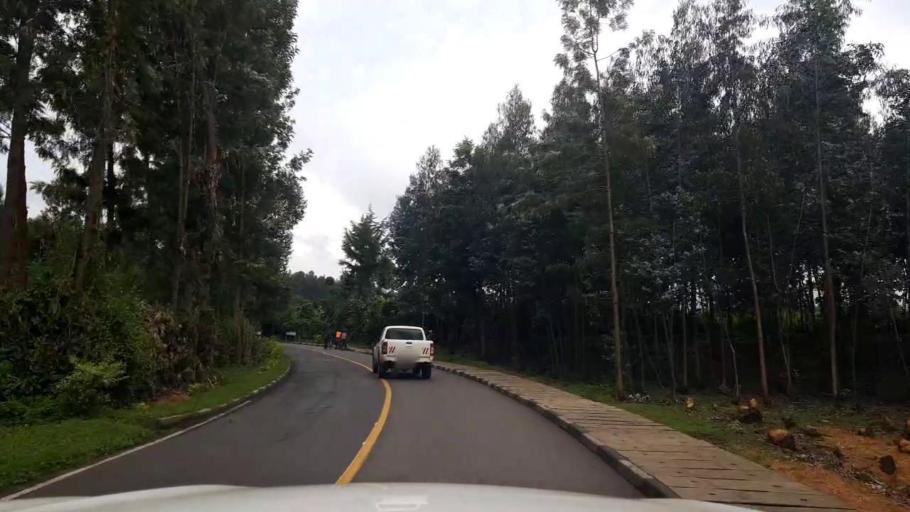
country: RW
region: Northern Province
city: Musanze
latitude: -1.4523
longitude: 29.6057
